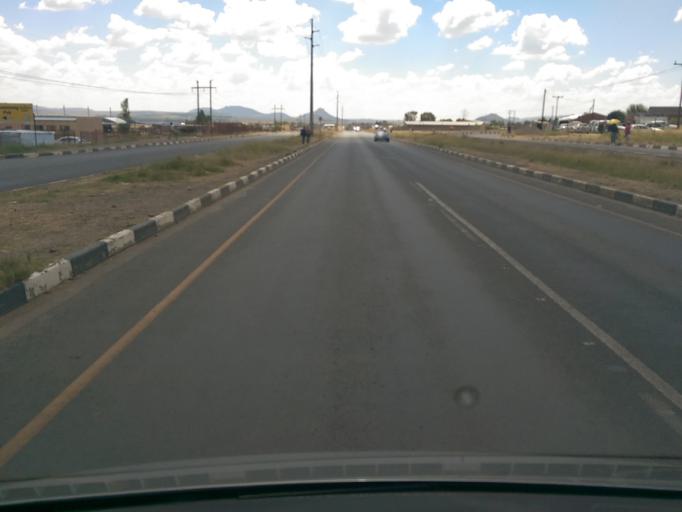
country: LS
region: Maseru
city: Maseru
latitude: -29.3623
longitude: 27.4660
